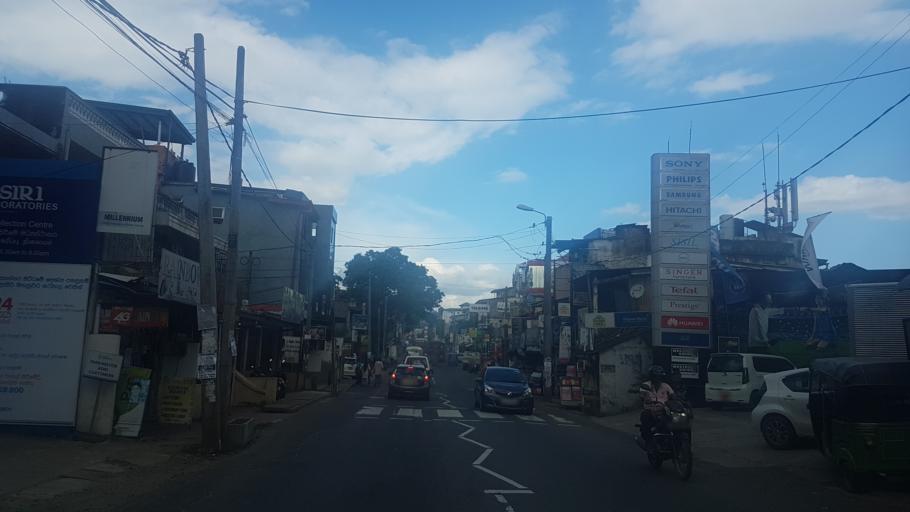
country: LK
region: Central
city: Kandy
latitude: 7.2887
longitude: 80.6291
